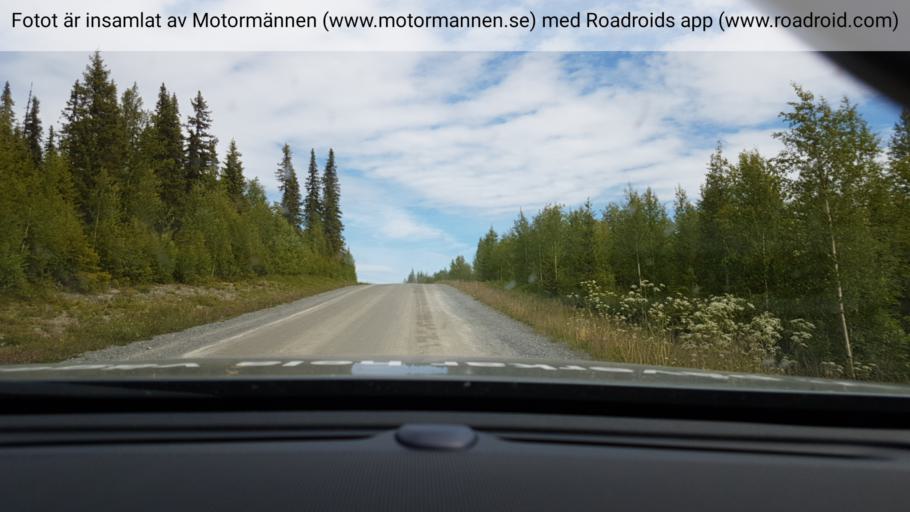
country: SE
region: Vaesterbotten
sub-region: Vilhelmina Kommun
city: Sjoberg
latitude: 65.1961
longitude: 16.1176
